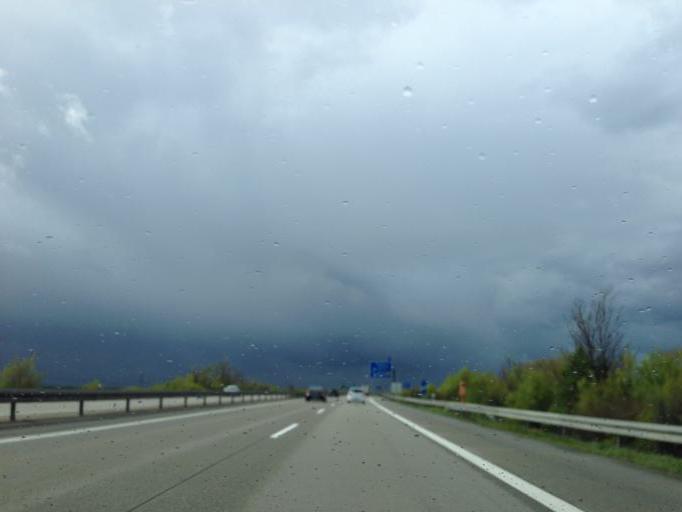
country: DE
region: Saxony-Anhalt
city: Diesdorf
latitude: 52.0669
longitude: 11.5653
